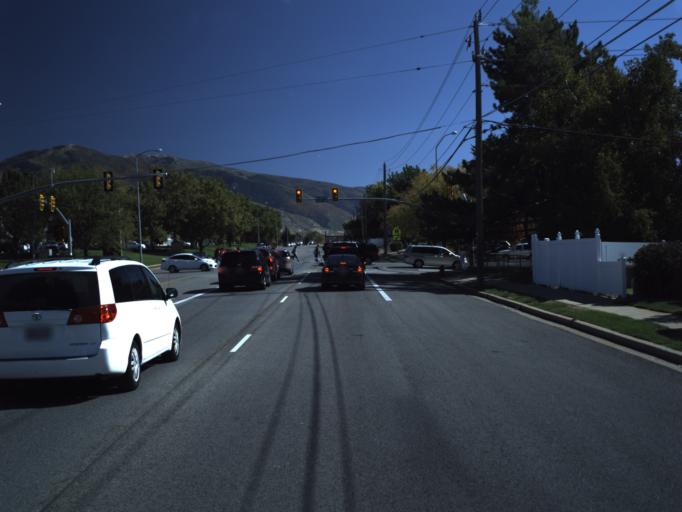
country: US
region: Utah
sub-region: Davis County
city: Kaysville
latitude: 41.0303
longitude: -111.9351
